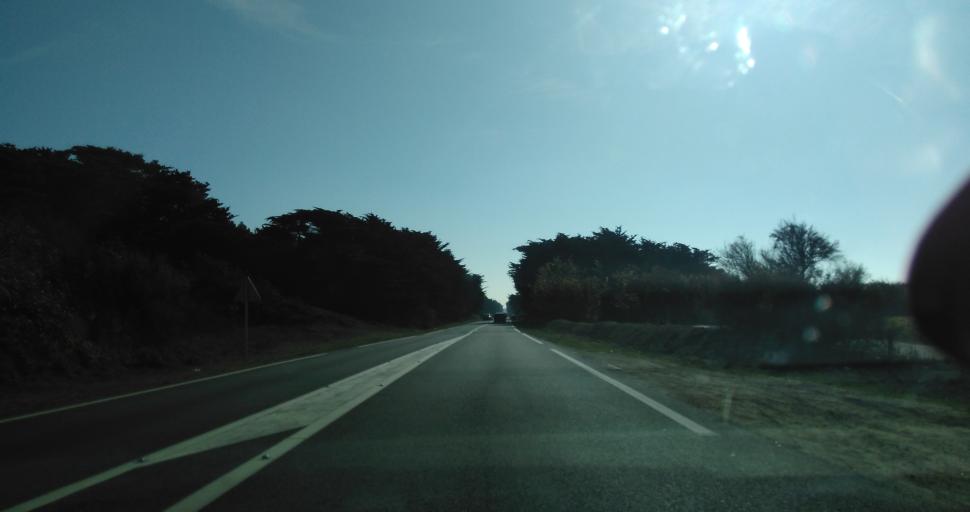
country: FR
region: Brittany
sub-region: Departement du Morbihan
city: Plouharnel
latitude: 47.5746
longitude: -3.1347
